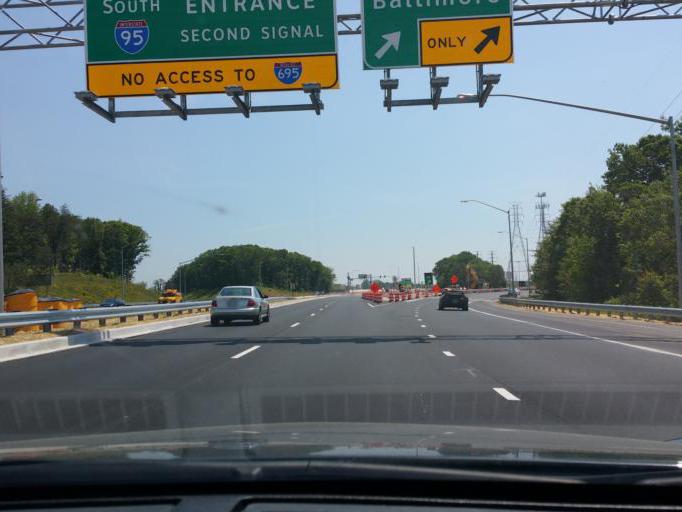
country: US
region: Maryland
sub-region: Baltimore County
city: White Marsh
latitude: 39.3794
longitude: -76.4561
